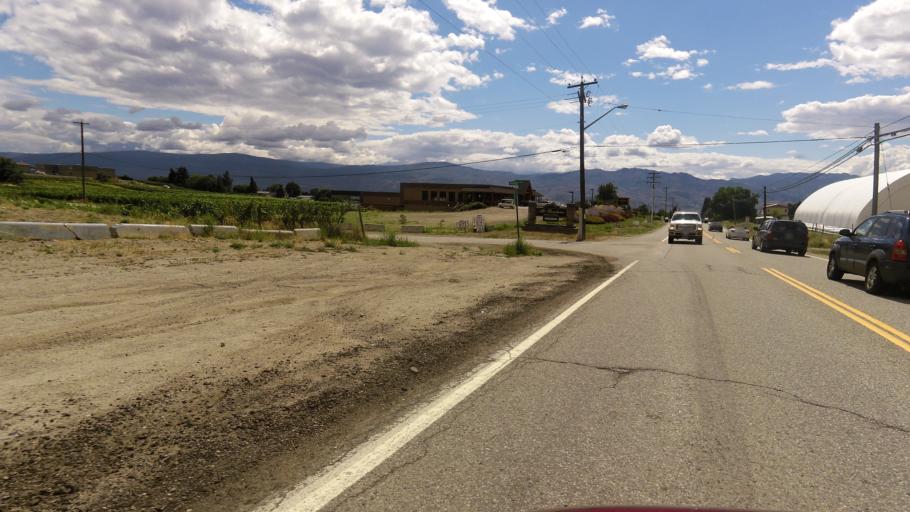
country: CA
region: British Columbia
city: West Kelowna
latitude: 49.8569
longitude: -119.5558
